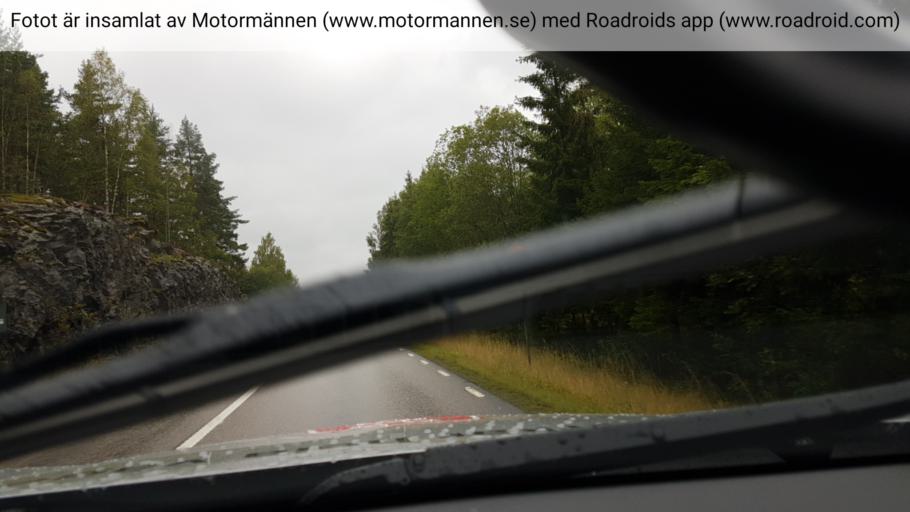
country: SE
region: Vaestra Goetaland
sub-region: Bengtsfors Kommun
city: Billingsfors
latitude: 58.9270
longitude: 12.2150
